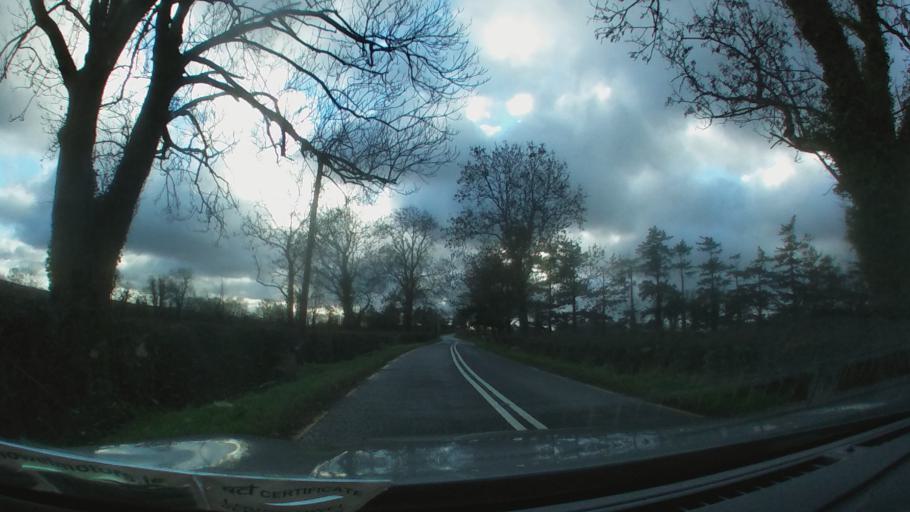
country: IE
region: Leinster
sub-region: Kilkenny
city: Thomastown
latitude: 52.5685
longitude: -7.1164
